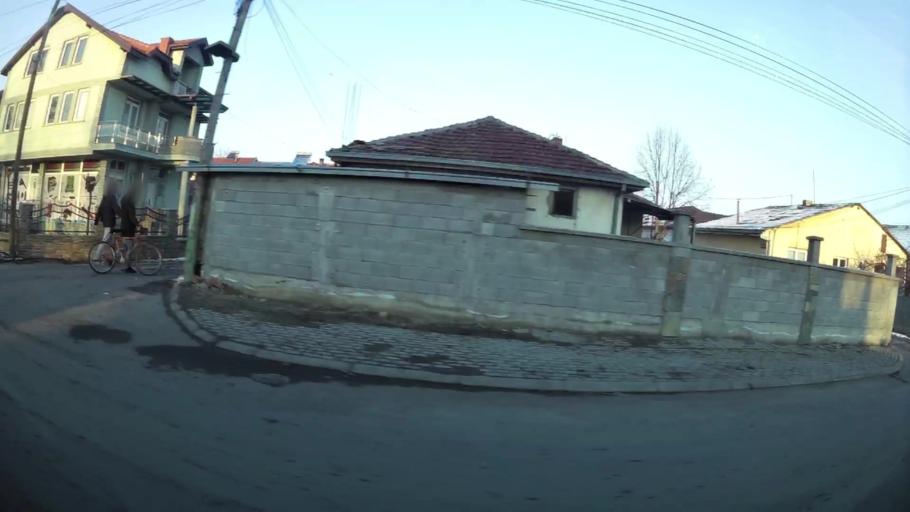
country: MK
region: Kisela Voda
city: Kisela Voda
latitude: 41.9756
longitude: 21.4860
